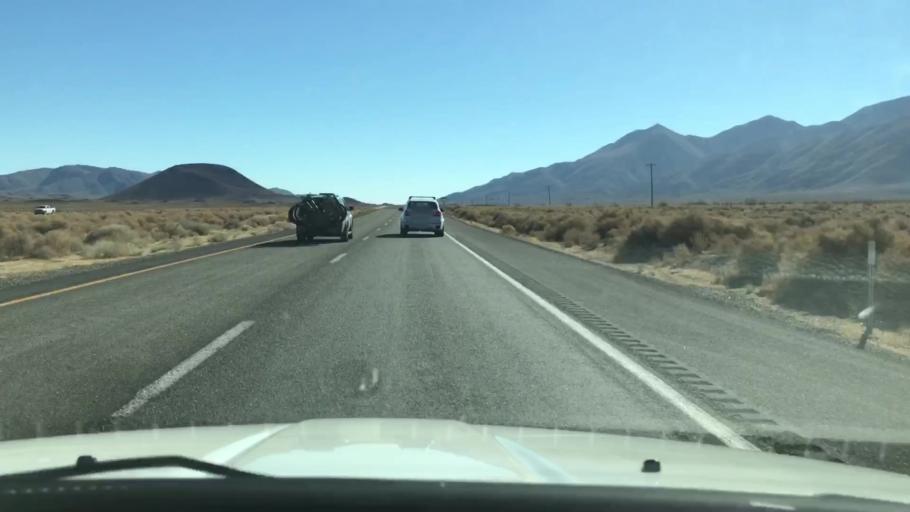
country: US
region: California
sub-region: Kern County
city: Inyokern
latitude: 36.0213
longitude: -117.9402
